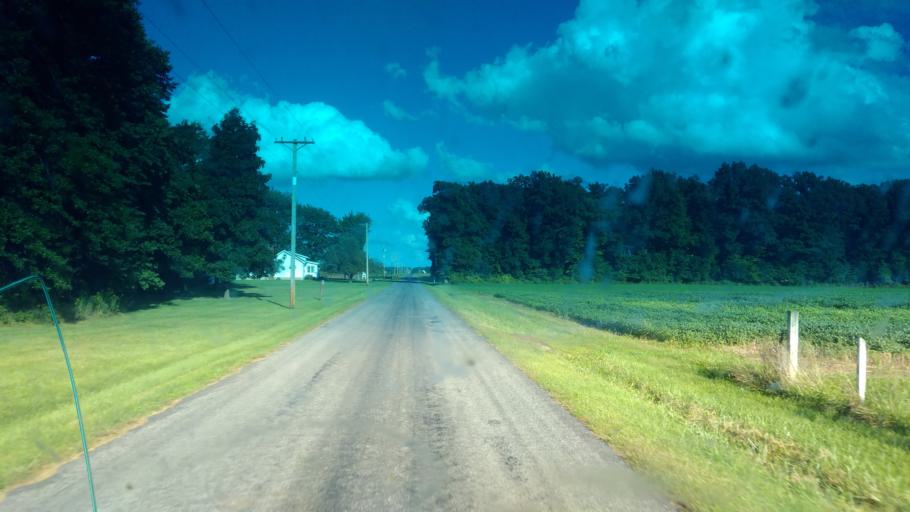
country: US
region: Ohio
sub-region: Hancock County
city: Arlington
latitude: 40.9362
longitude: -83.7137
